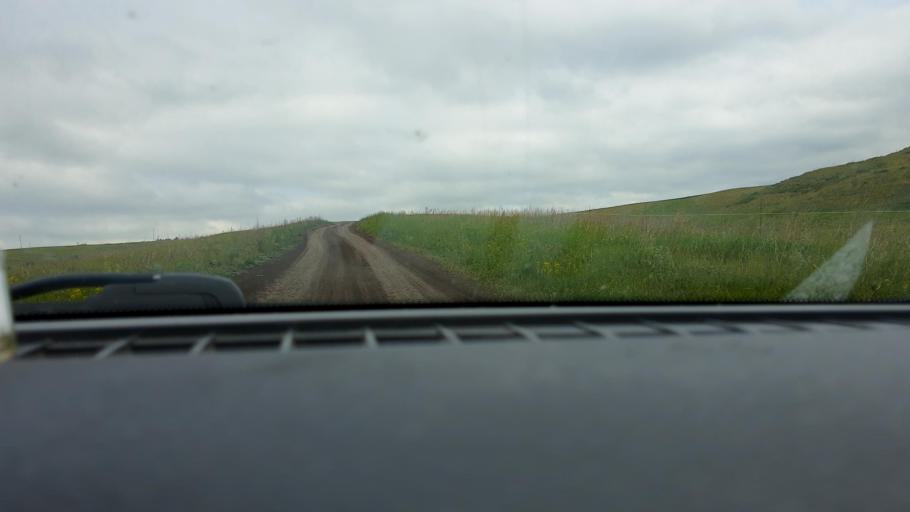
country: RU
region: Bashkortostan
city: Chishmy
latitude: 54.6879
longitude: 55.4837
